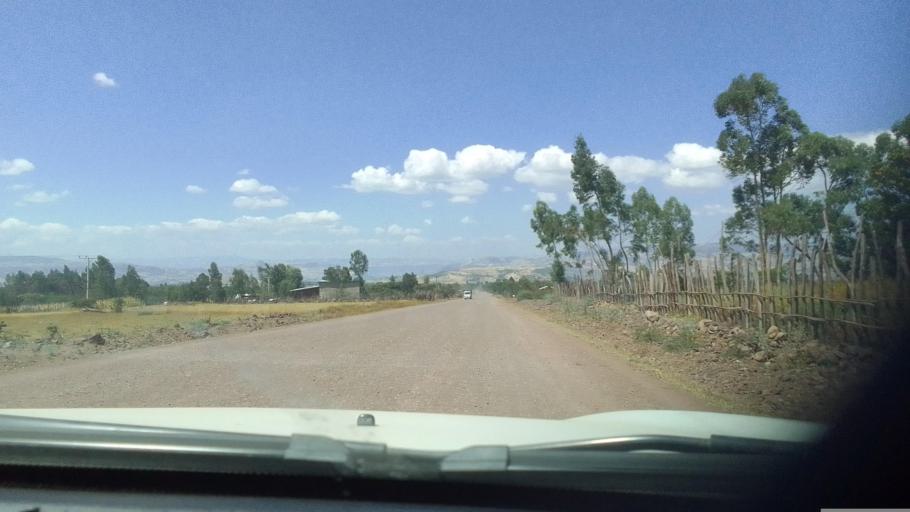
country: ET
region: Oromiya
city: Hagere Hiywet
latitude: 8.9255
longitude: 37.8623
